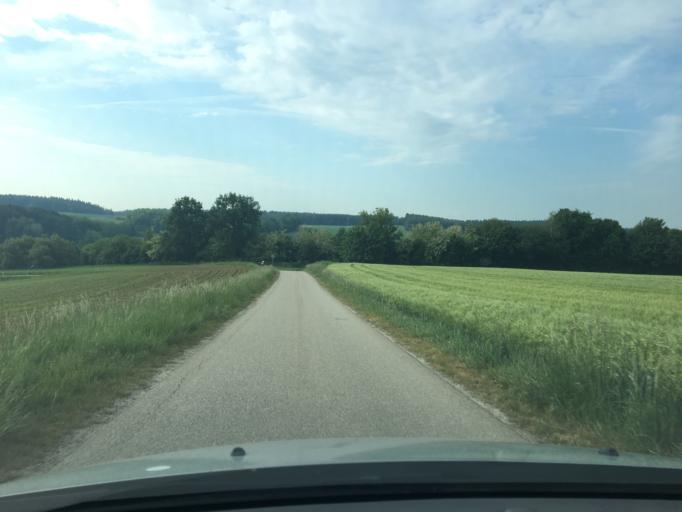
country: DE
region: Bavaria
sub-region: Upper Bavaria
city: Egglkofen
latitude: 48.4004
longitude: 12.4271
